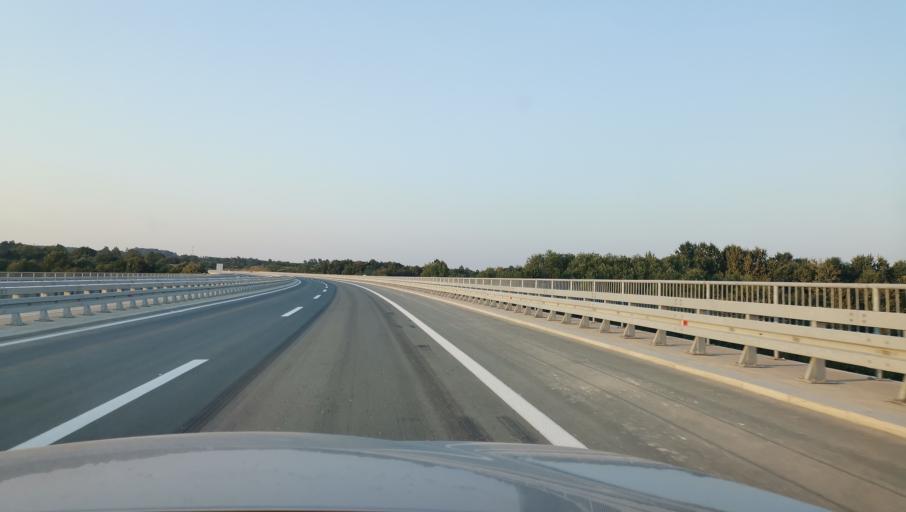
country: RS
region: Central Serbia
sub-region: Kolubarski Okrug
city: Ub
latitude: 44.4160
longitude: 20.1036
